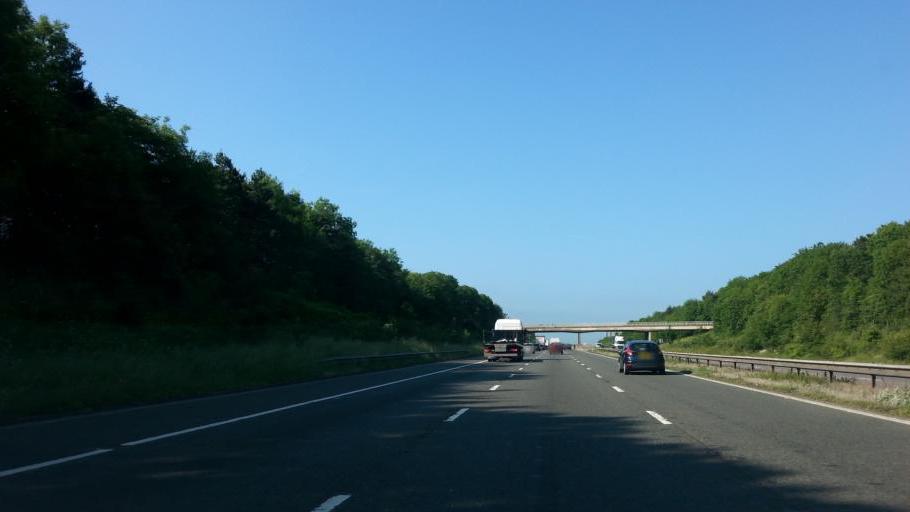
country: GB
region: England
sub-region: Gloucestershire
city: Churchdown
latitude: 51.8707
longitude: -2.1567
